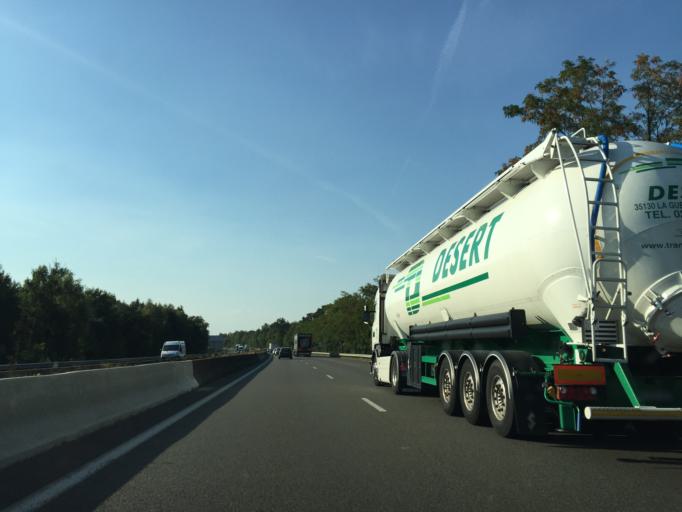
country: FR
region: Alsace
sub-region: Departement du Bas-Rhin
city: Vendenheim
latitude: 48.6920
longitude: 7.7260
